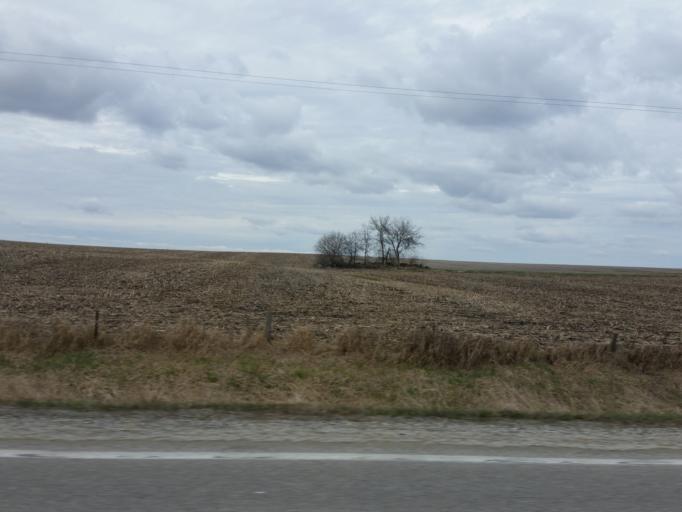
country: US
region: Iowa
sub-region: Black Hawk County
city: Evansdale
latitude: 42.5704
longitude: -92.2668
